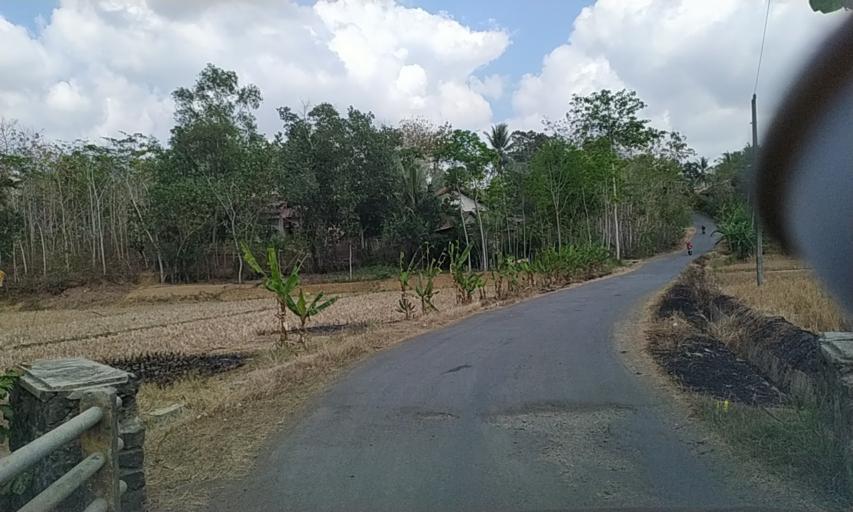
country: ID
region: Central Java
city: Prapagan
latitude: -7.5711
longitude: 109.0148
